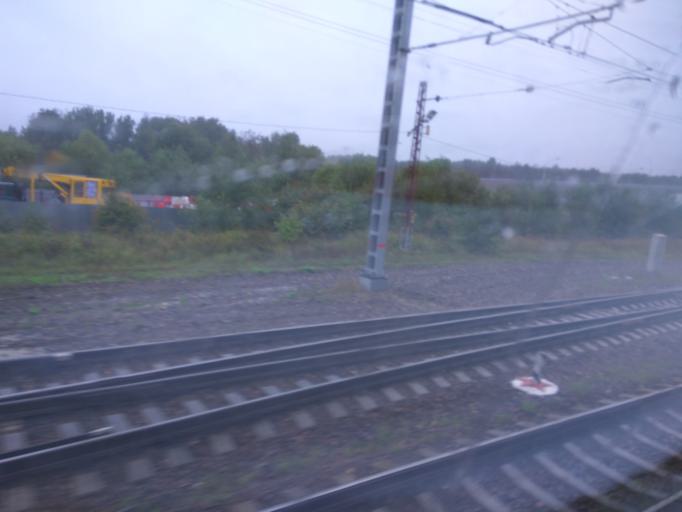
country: RU
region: Moskovskaya
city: Zhilevo
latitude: 54.9926
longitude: 38.0280
